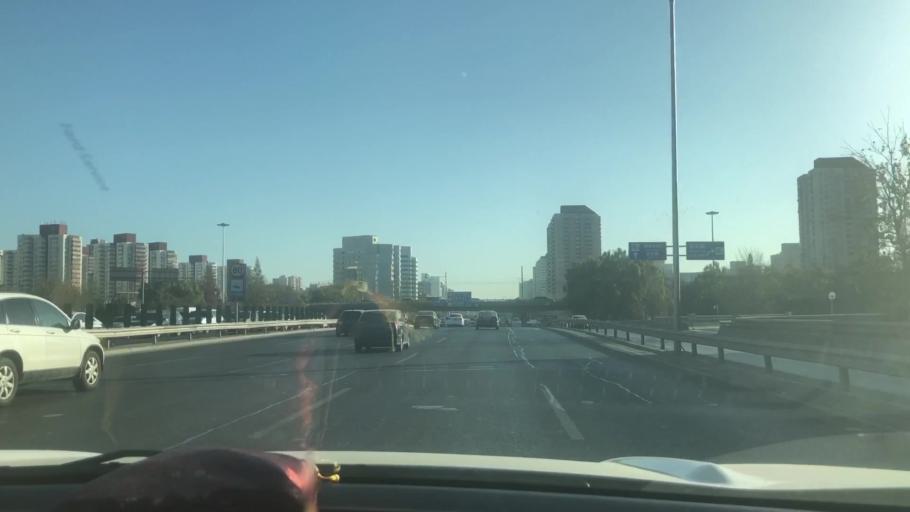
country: CN
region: Beijing
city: Datun
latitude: 39.9868
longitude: 116.3990
